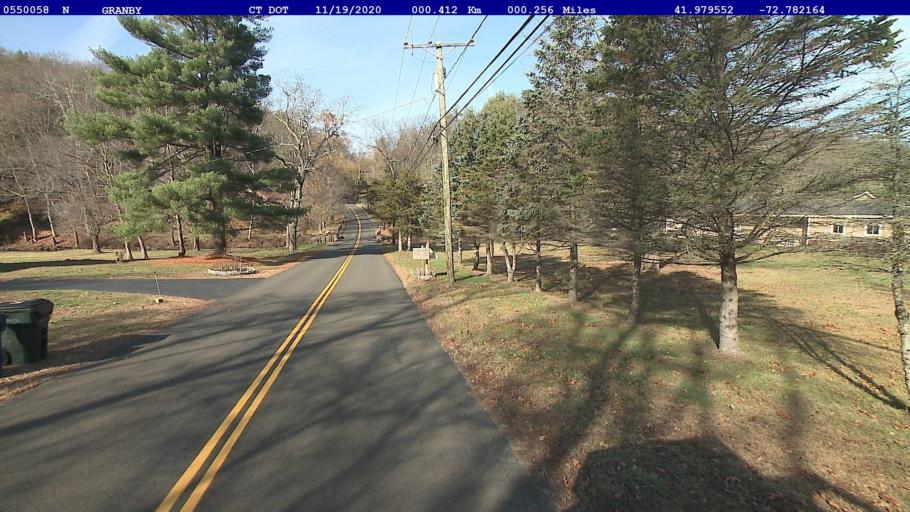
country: US
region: Connecticut
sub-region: Hartford County
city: Salmon Brook
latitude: 41.9796
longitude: -72.7822
